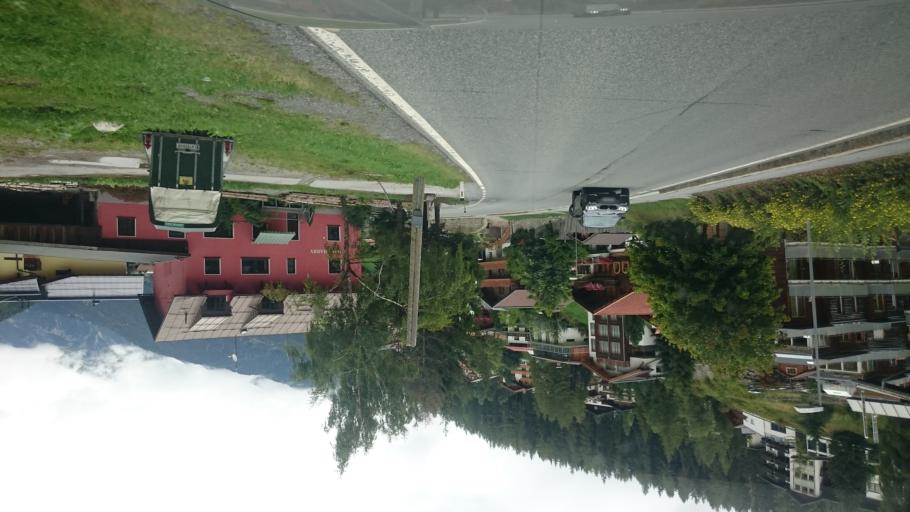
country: AT
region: Tyrol
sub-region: Politischer Bezirk Landeck
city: Sankt Anton am Arlberg
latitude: 47.1226
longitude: 10.2539
